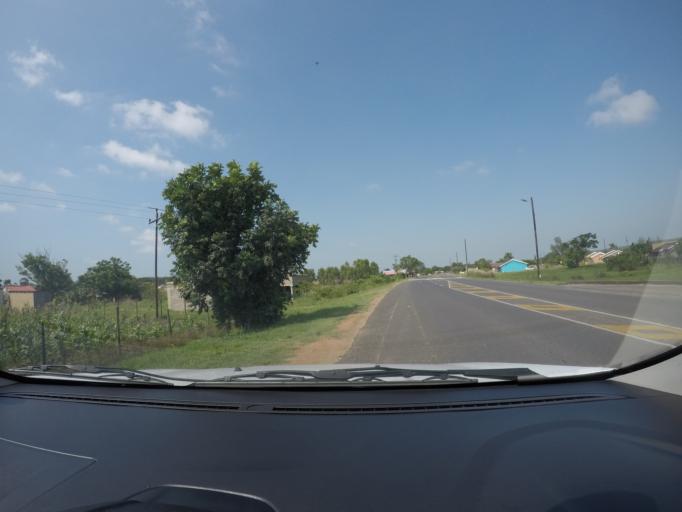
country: ZA
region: KwaZulu-Natal
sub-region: uThungulu District Municipality
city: eSikhawini
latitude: -28.8916
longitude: 31.8908
